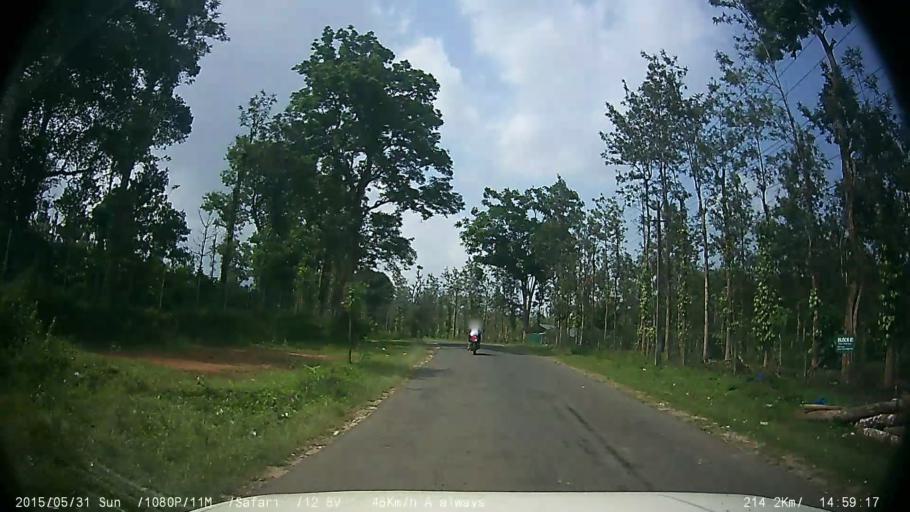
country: IN
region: Kerala
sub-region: Wayanad
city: Kalpetta
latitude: 11.6093
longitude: 76.2098
